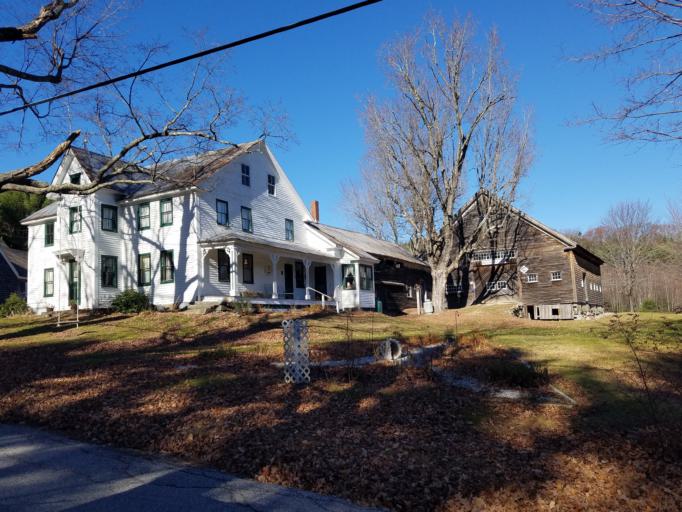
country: US
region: New Hampshire
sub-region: Carroll County
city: Ossipee
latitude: 43.6798
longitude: -71.0311
